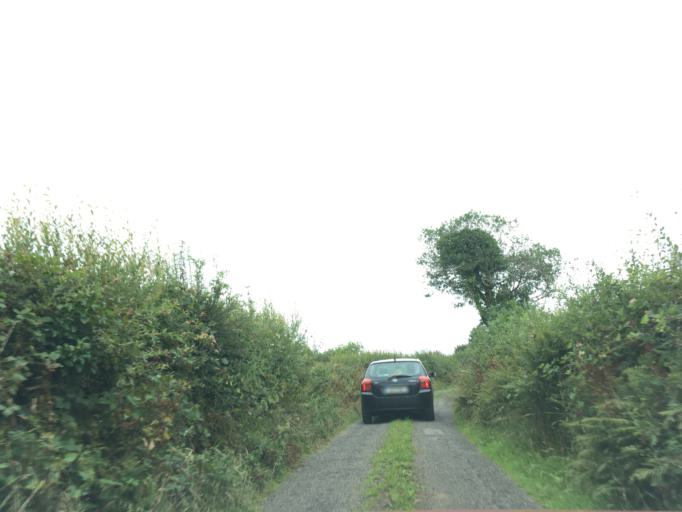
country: IE
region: Munster
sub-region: An Clar
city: Ennis
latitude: 52.7272
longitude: -9.0901
